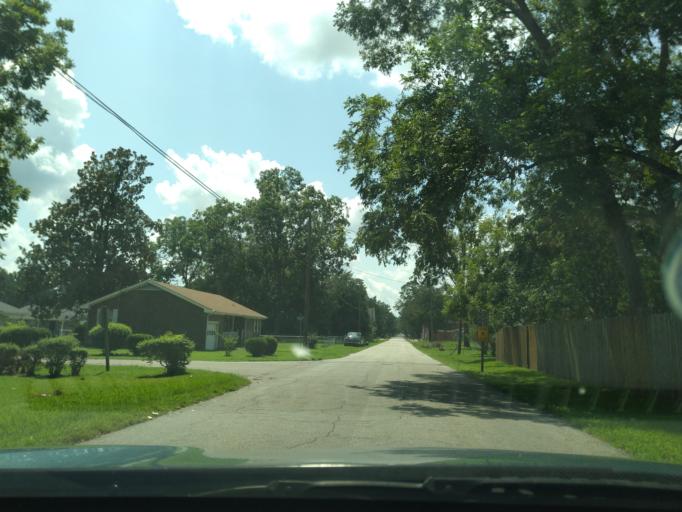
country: US
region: North Carolina
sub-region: Washington County
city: Plymouth
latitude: 35.8667
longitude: -76.7452
